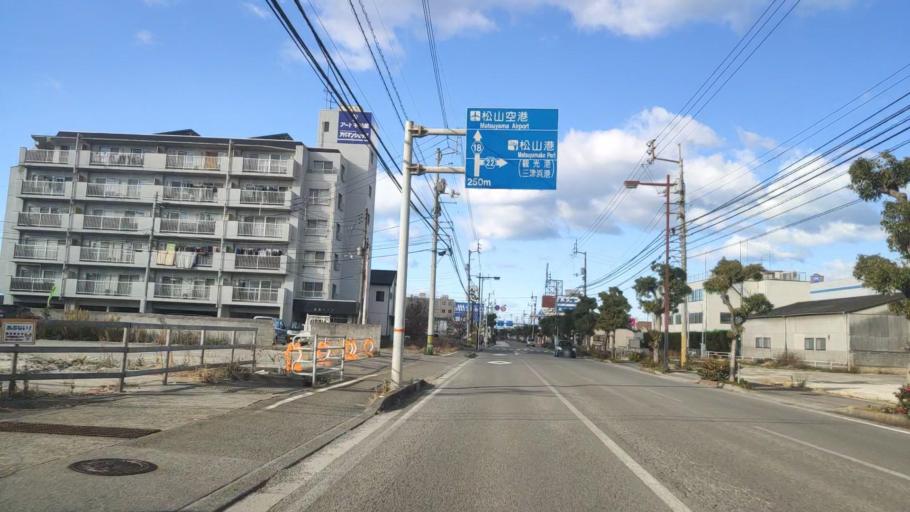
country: JP
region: Ehime
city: Masaki-cho
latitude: 33.8282
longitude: 132.7119
